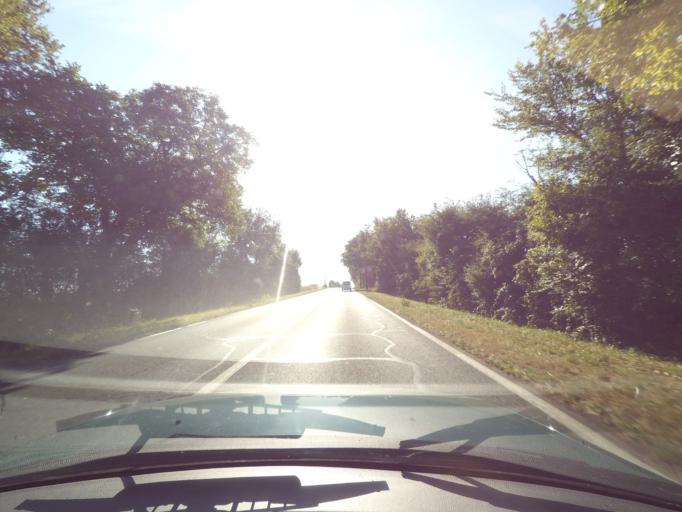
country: FR
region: Poitou-Charentes
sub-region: Departement de la Vienne
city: Ayron
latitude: 46.6588
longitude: 0.0856
